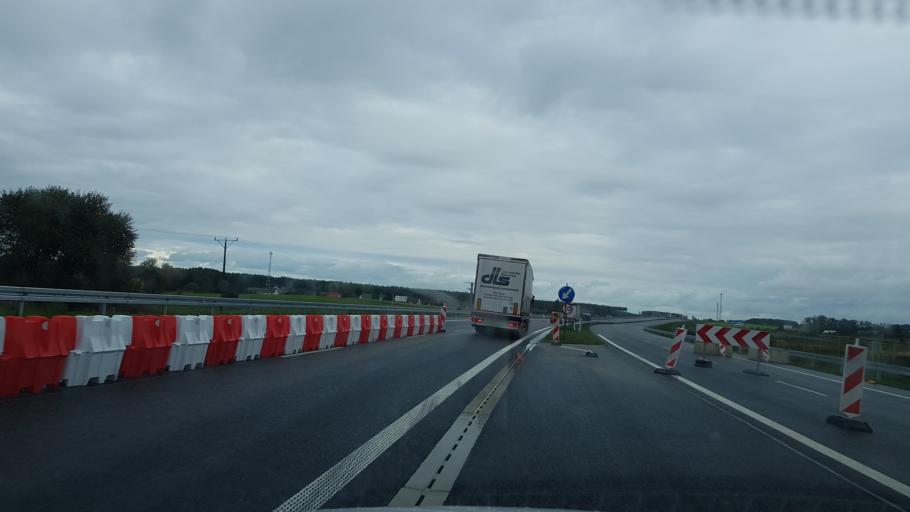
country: PL
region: West Pomeranian Voivodeship
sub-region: Powiat goleniowski
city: Przybiernow
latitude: 53.7524
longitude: 14.7733
